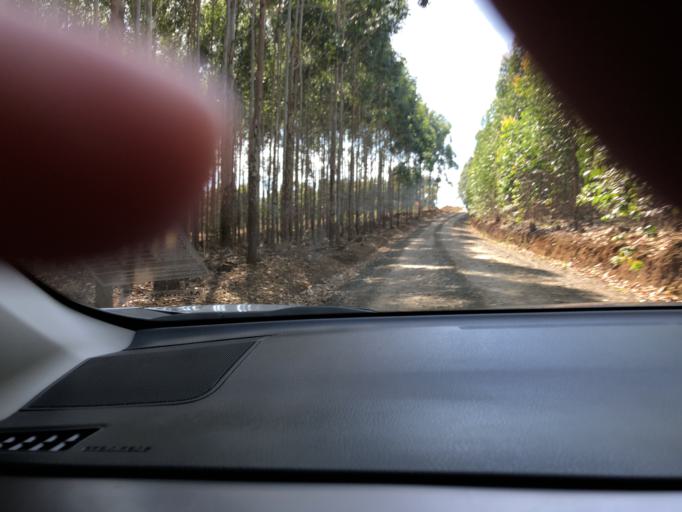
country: ZA
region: KwaZulu-Natal
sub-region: Sisonke District Municipality
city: Ixopo
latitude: -30.1828
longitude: 30.0545
